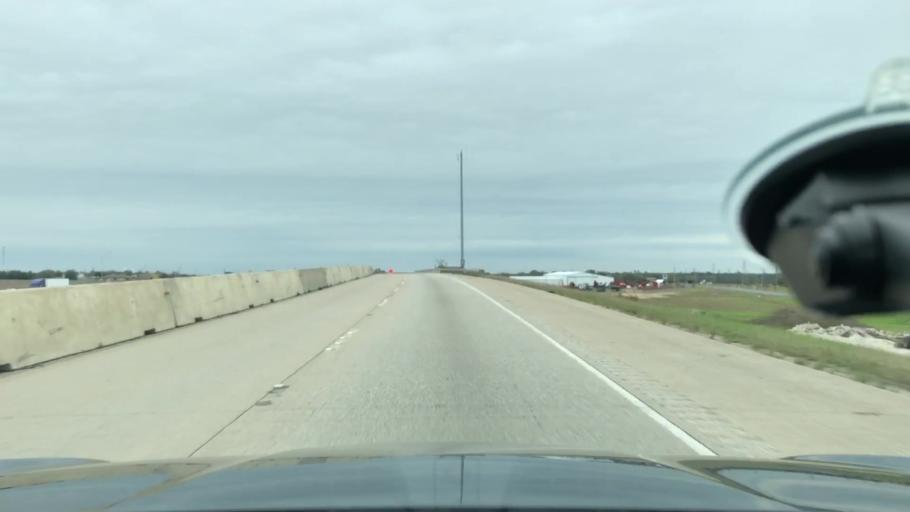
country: US
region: Texas
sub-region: Ellis County
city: Waxahachie
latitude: 32.3620
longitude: -96.8553
